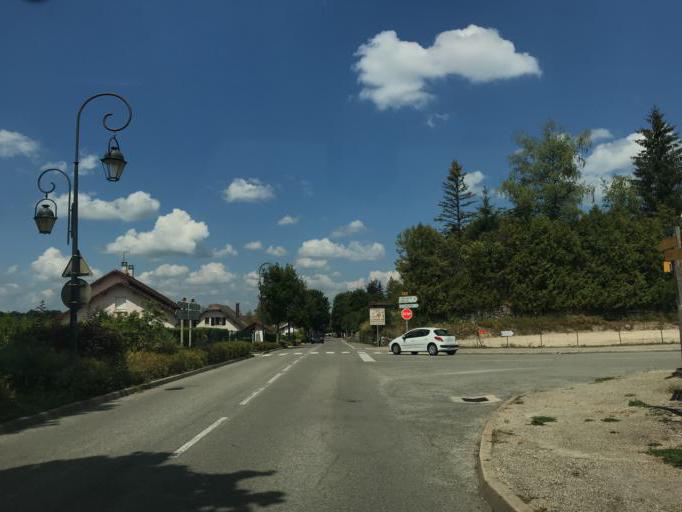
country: FR
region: Franche-Comte
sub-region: Departement du Jura
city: Clairvaux-les-Lacs
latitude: 46.5730
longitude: 5.7535
